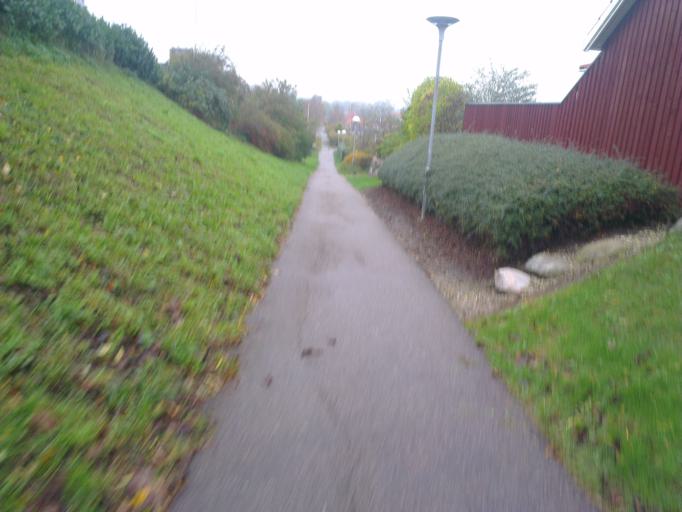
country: DK
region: Capital Region
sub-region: Frederikssund Kommune
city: Jaegerspris
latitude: 55.8519
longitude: 11.9971
